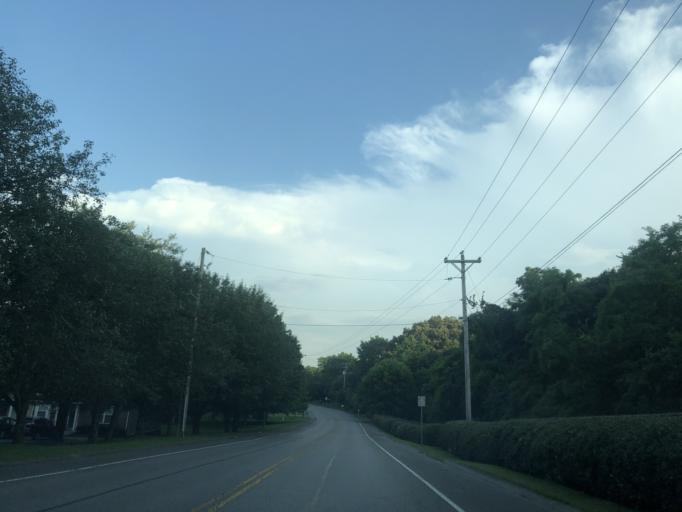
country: US
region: Tennessee
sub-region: Davidson County
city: Lakewood
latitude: 36.1367
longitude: -86.6411
